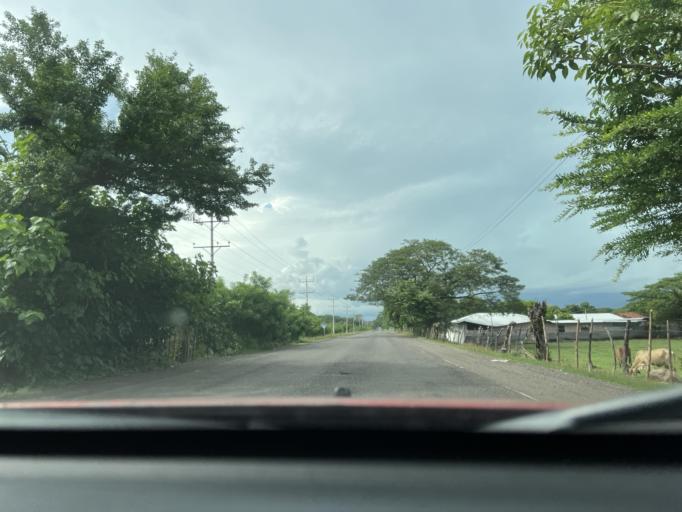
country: SV
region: La Union
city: La Union
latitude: 13.3786
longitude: -87.9078
